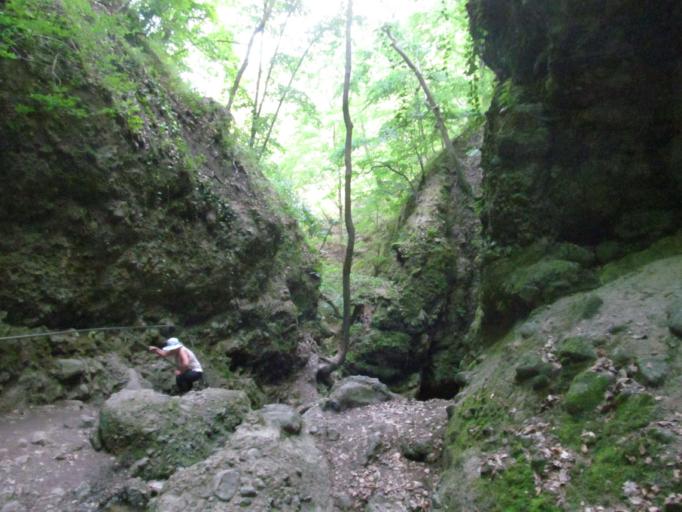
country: HU
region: Pest
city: Pilisszentkereszt
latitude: 47.7378
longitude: 18.8934
